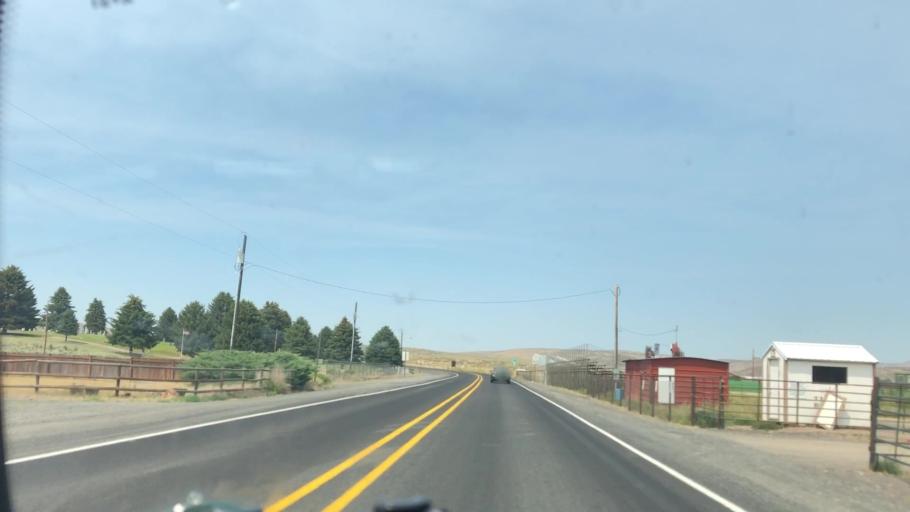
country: US
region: Idaho
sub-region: Owyhee County
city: Murphy
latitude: 42.9804
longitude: -117.0531
